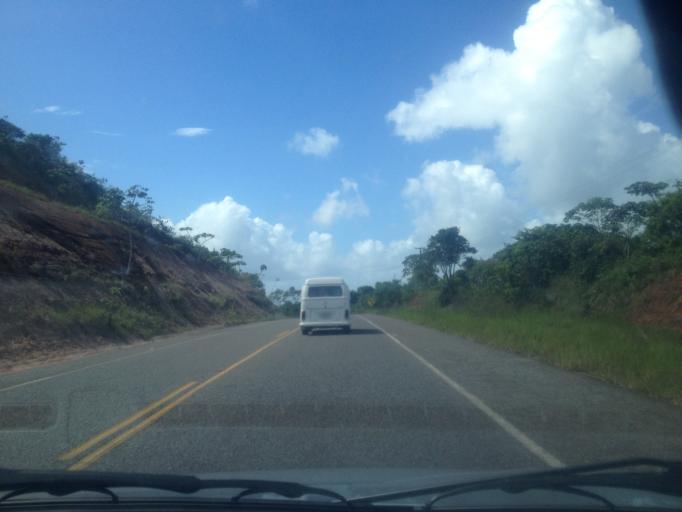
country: BR
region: Bahia
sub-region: Conde
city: Conde
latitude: -11.7726
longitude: -37.5943
